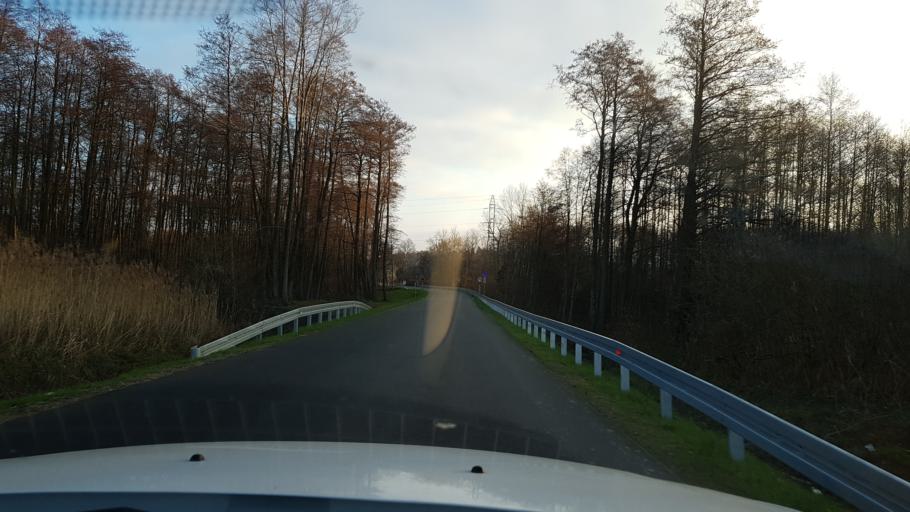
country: PL
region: West Pomeranian Voivodeship
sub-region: Koszalin
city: Koszalin
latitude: 54.1248
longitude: 16.0908
